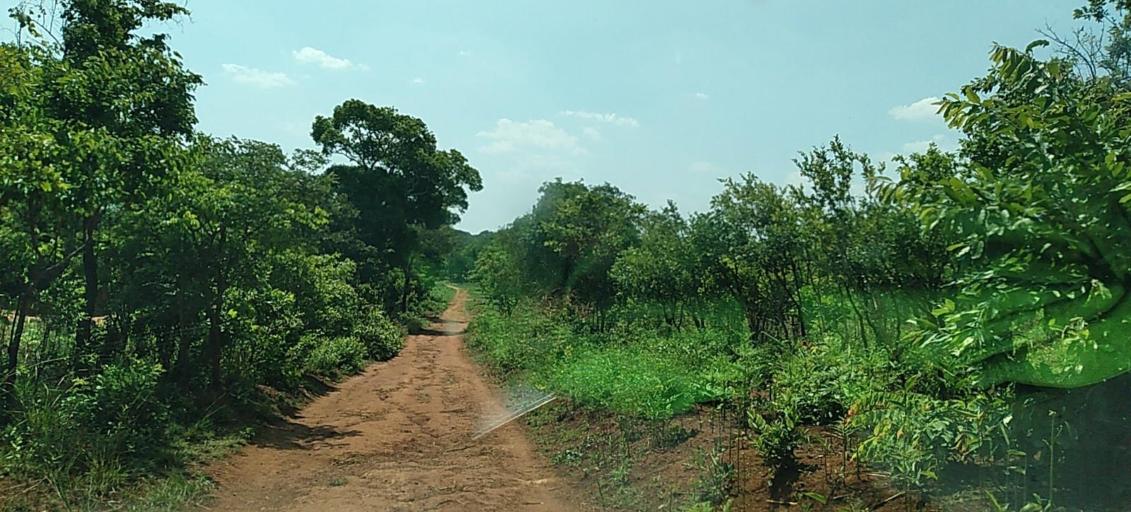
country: CD
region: Katanga
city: Kolwezi
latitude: -11.2804
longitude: 25.1358
